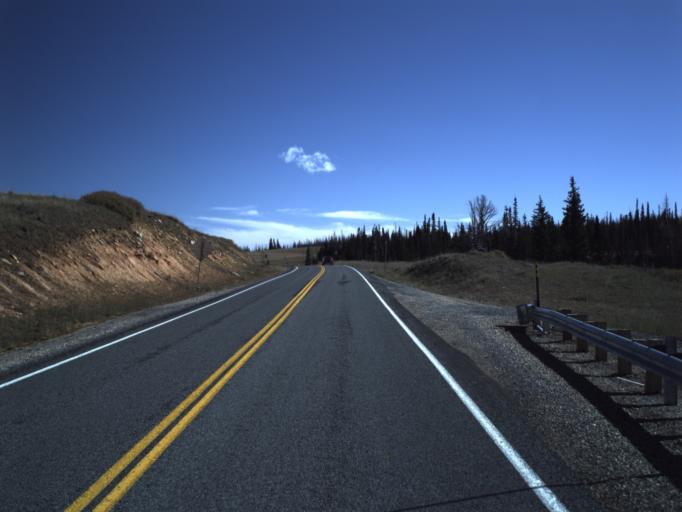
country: US
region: Utah
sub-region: Iron County
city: Parowan
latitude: 37.6740
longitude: -112.8416
